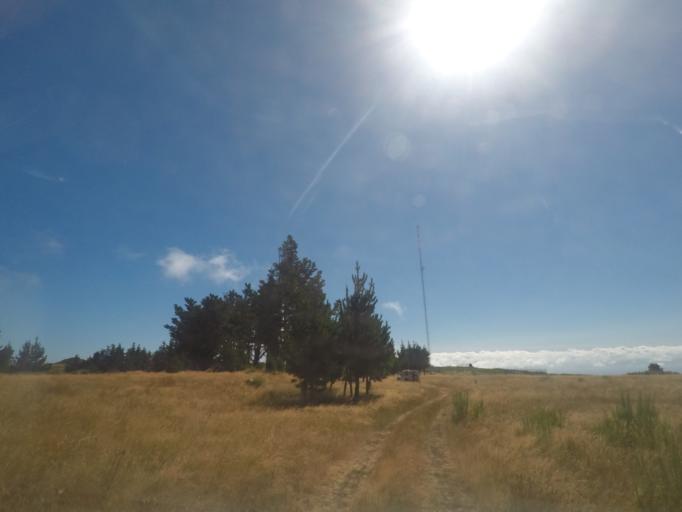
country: PT
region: Madeira
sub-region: Funchal
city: Nossa Senhora do Monte
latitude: 32.7100
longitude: -16.9098
